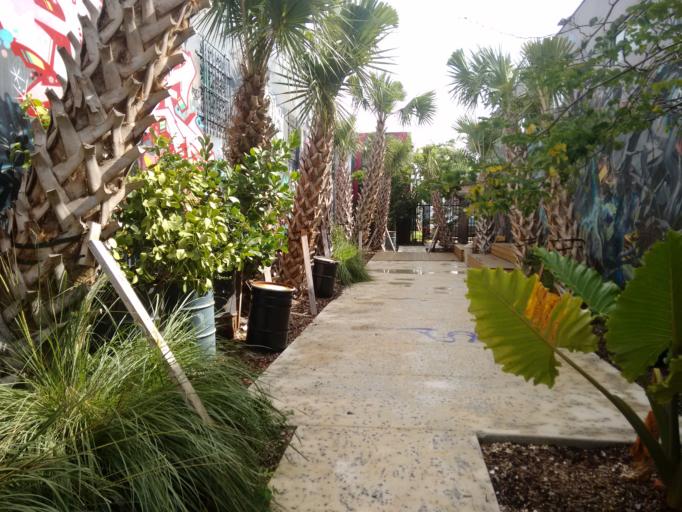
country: US
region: Florida
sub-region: Miami-Dade County
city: Allapattah
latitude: 25.8013
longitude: -80.2021
